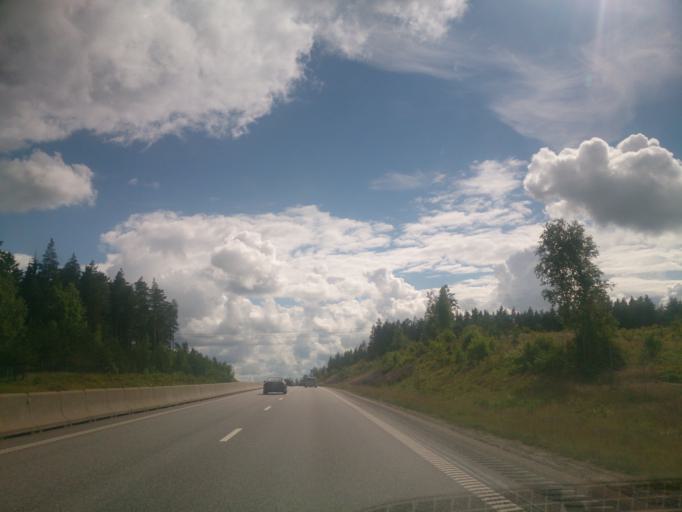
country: SE
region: OEstergoetland
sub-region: Norrkopings Kommun
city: Kimstad
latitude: 58.5170
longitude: 15.9978
